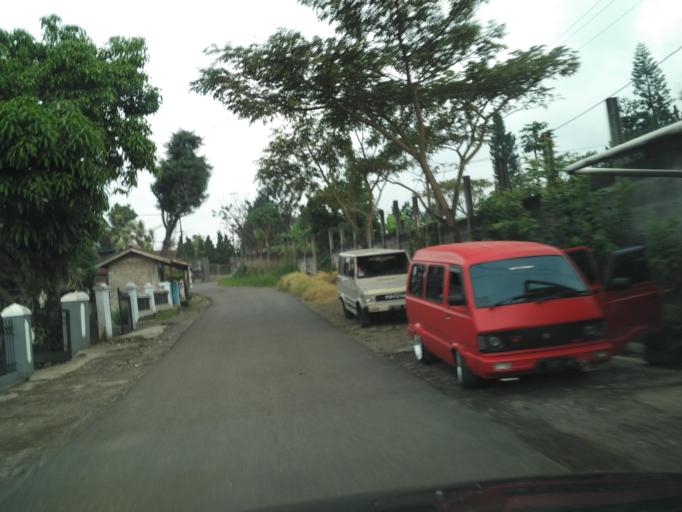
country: ID
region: West Java
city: Caringin
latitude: -6.7016
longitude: 107.0359
